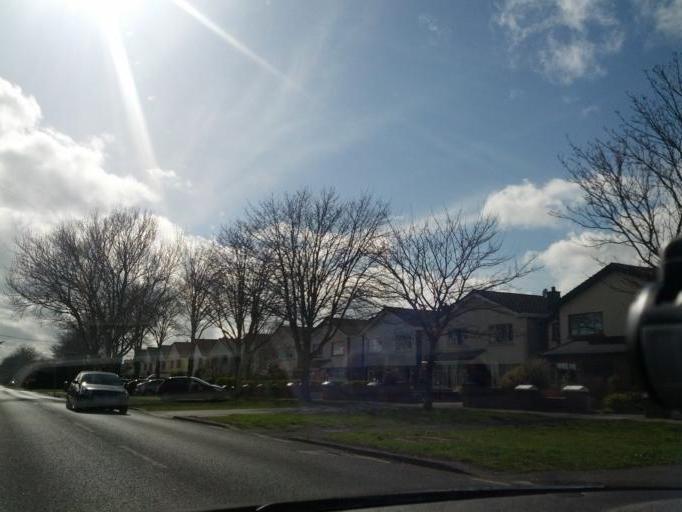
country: IE
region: Leinster
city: Portmarnock
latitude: 53.4267
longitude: -6.1304
